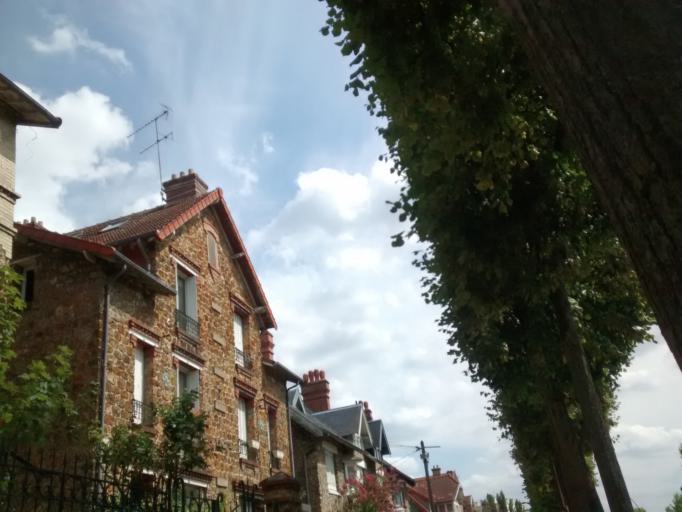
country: FR
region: Ile-de-France
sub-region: Departement des Yvelines
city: Viroflay
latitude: 48.8052
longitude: 2.1520
